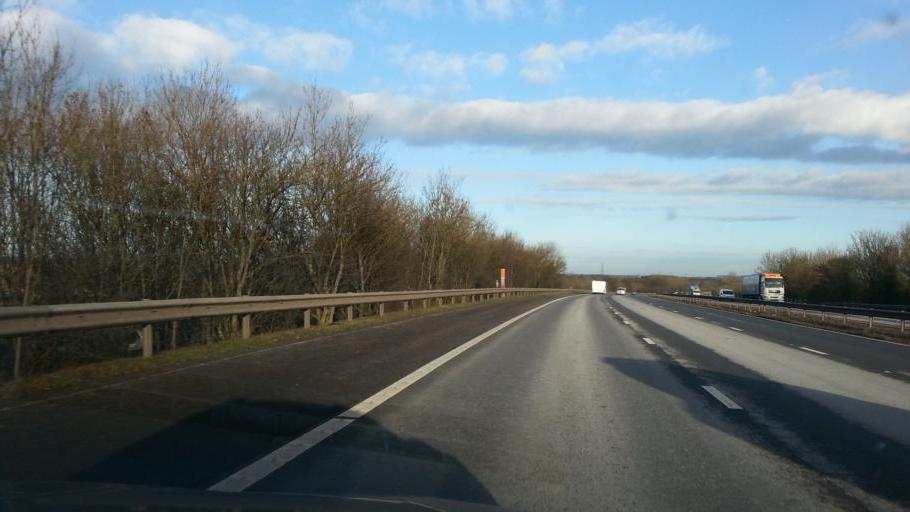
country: GB
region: England
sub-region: Leicestershire
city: Stoney Stanton
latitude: 52.5607
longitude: -1.2961
